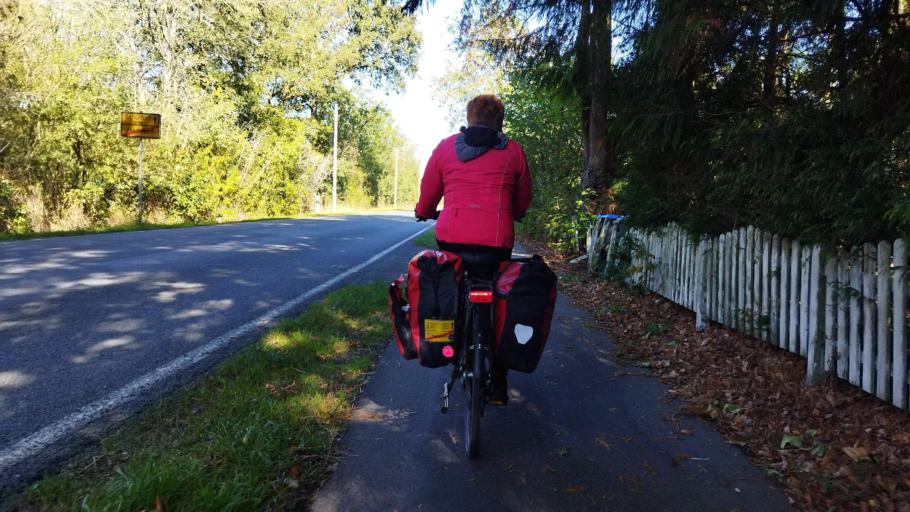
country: DE
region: Lower Saxony
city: Ohne
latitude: 52.2585
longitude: 7.3151
